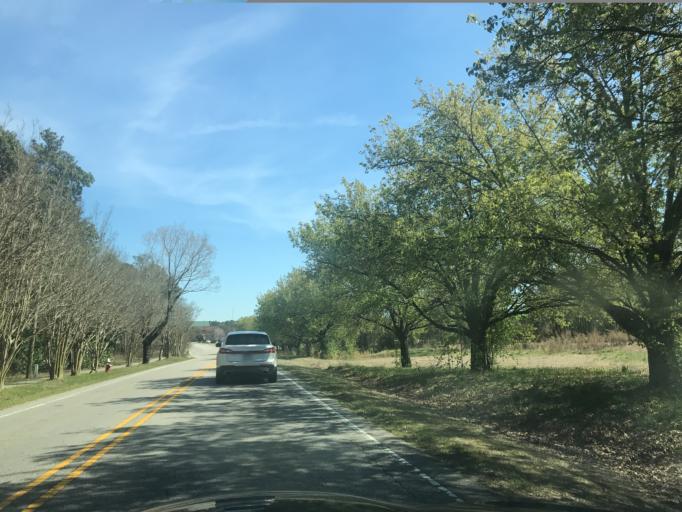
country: US
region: North Carolina
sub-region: Wake County
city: Fuquay-Varina
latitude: 35.5956
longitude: -78.7974
